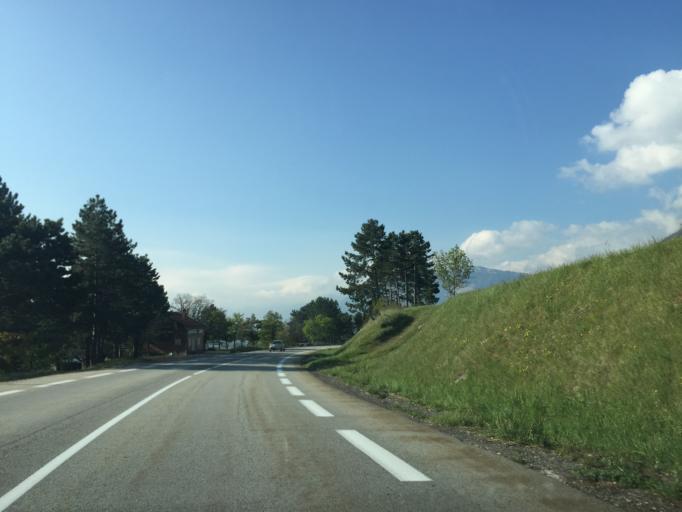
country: FR
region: Rhone-Alpes
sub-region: Departement de l'Isere
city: La Motte-Saint-Martin
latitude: 44.8766
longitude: 5.6255
